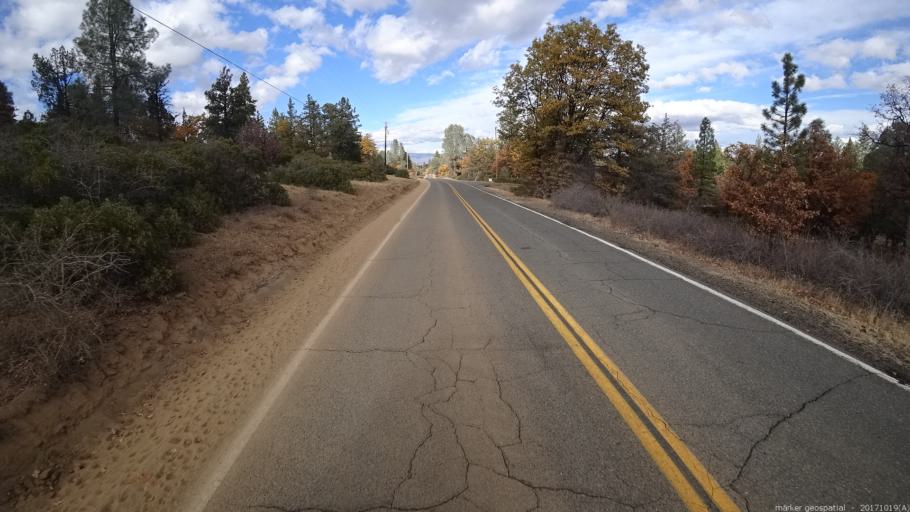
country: US
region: California
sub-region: Shasta County
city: Burney
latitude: 40.9601
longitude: -121.4383
